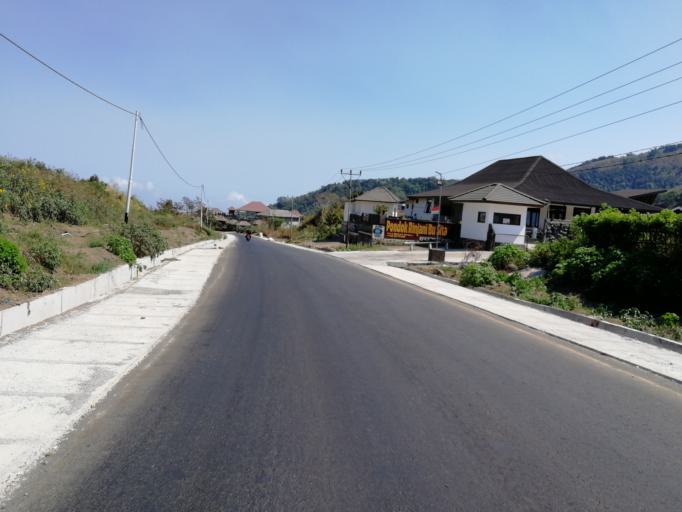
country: ID
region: West Nusa Tenggara
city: Sembalunlawang
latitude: -8.3554
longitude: 116.5139
